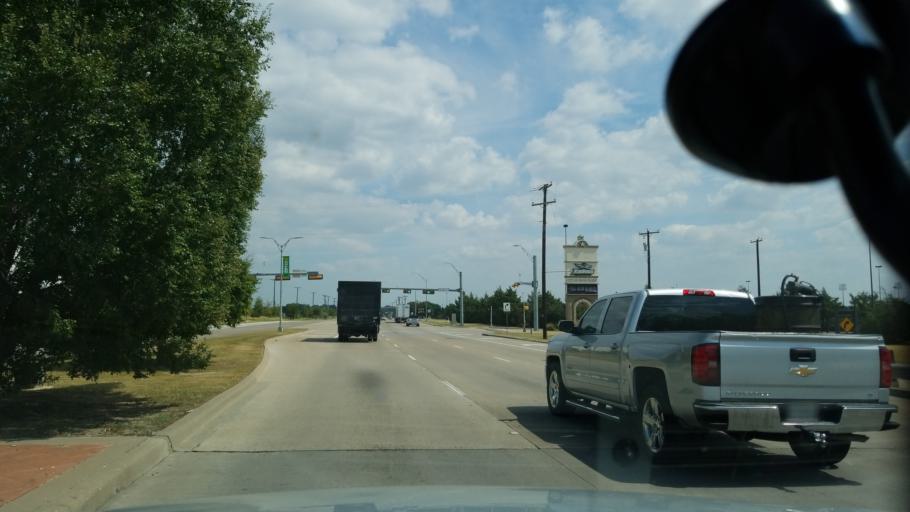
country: US
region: Texas
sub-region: Dallas County
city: Grand Prairie
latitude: 32.7691
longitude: -96.9949
